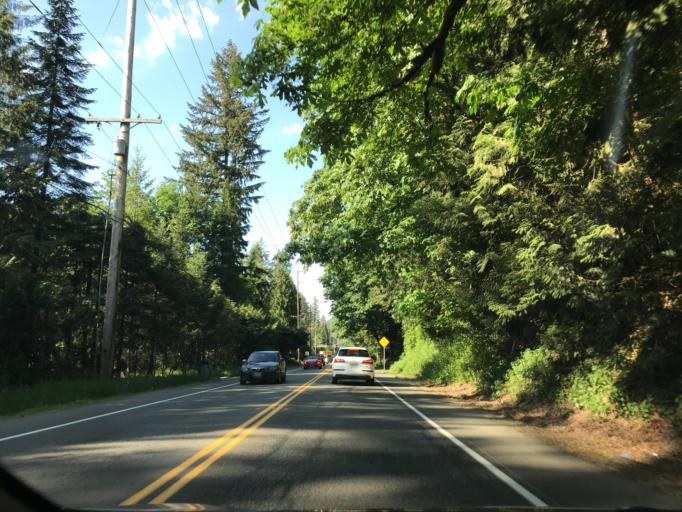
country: US
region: Washington
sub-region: King County
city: Mirrormont
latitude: 47.4827
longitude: -122.0281
